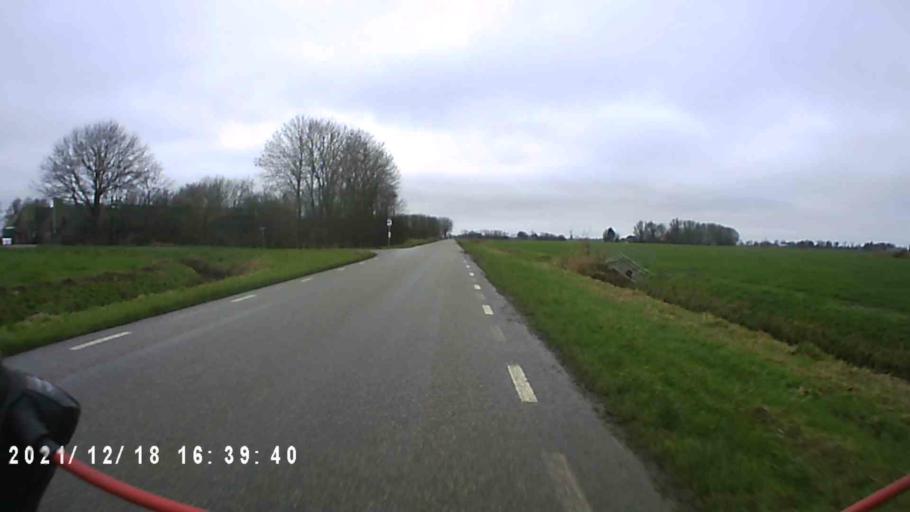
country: NL
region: Friesland
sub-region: Gemeente Dongeradeel
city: Dokkum
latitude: 53.3603
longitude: 6.0058
